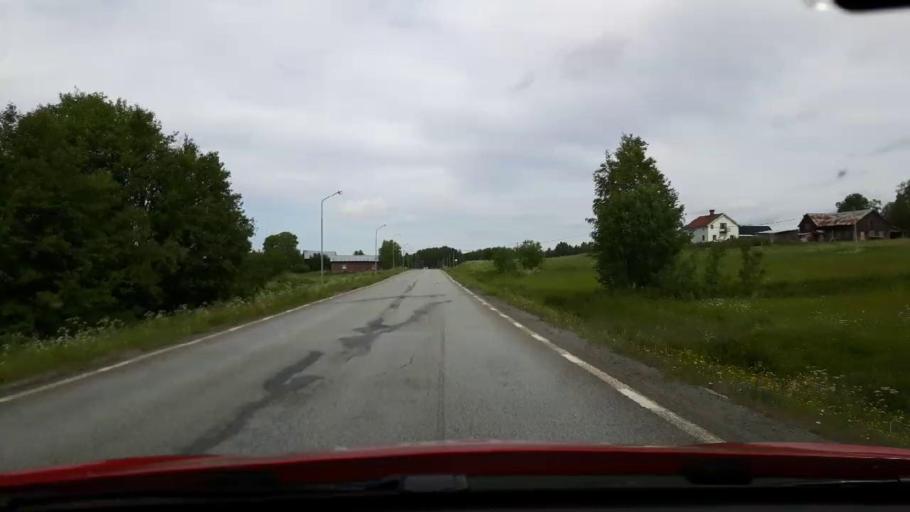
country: SE
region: Jaemtland
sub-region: Bergs Kommun
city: Hoverberg
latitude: 63.0116
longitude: 14.4930
